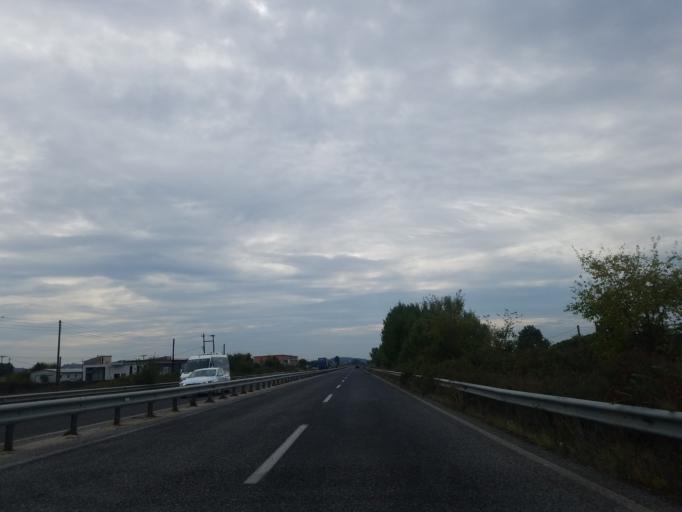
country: GR
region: Thessaly
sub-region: Trikala
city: Vasiliki
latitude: 39.6070
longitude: 21.7246
